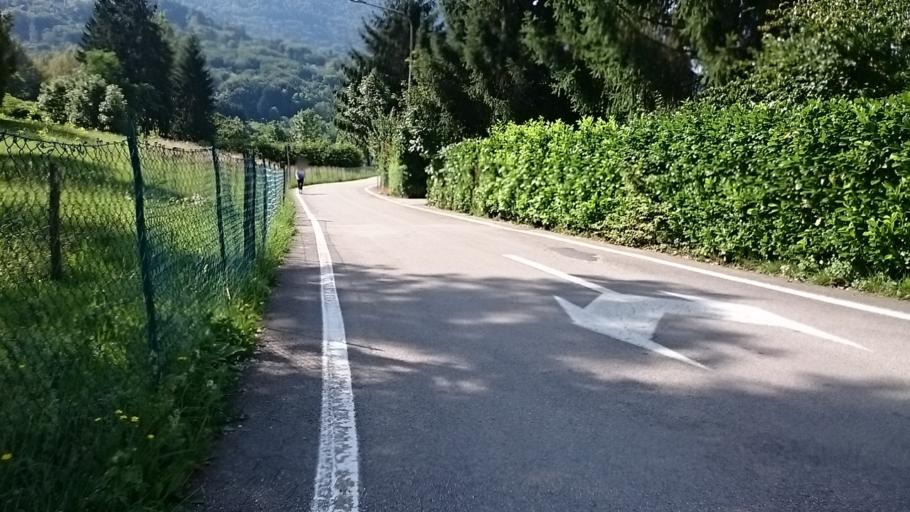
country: IT
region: Veneto
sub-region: Provincia di Belluno
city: Farra d'Alpago
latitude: 46.1196
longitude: 12.3545
